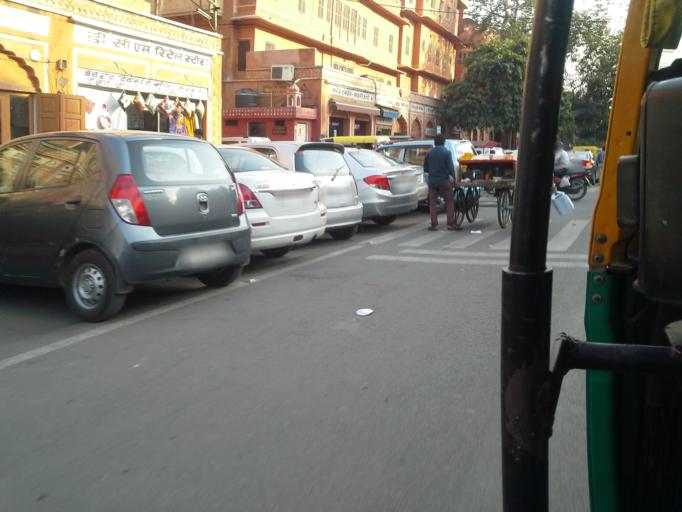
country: IN
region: Rajasthan
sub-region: Jaipur
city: Jaipur
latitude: 26.9190
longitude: 75.8214
